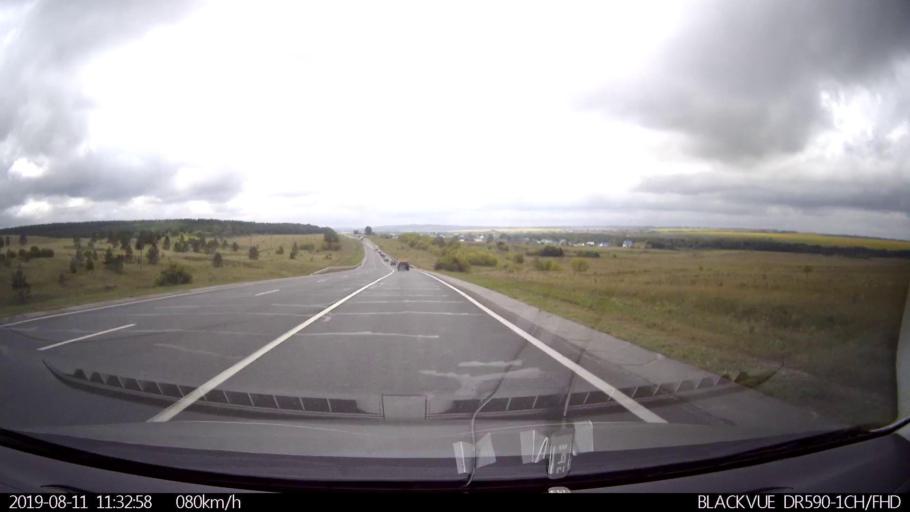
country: RU
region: Ulyanovsk
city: Krasnyy Gulyay
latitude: 54.0323
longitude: 48.2126
